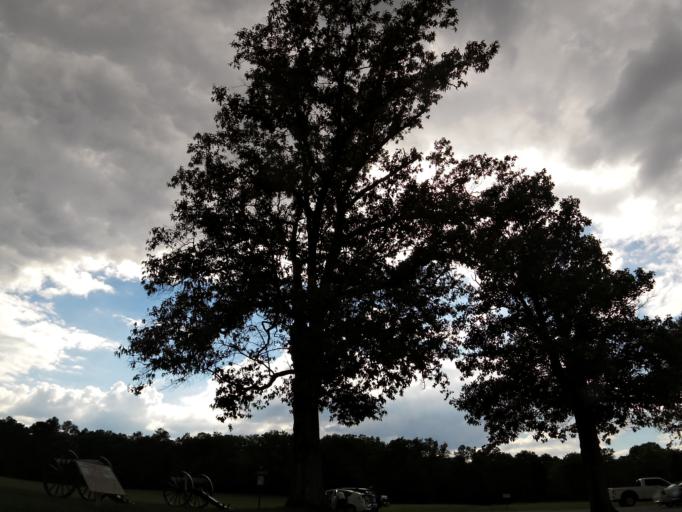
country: US
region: Georgia
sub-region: Catoosa County
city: Fort Oglethorpe
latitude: 34.9378
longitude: -85.2594
